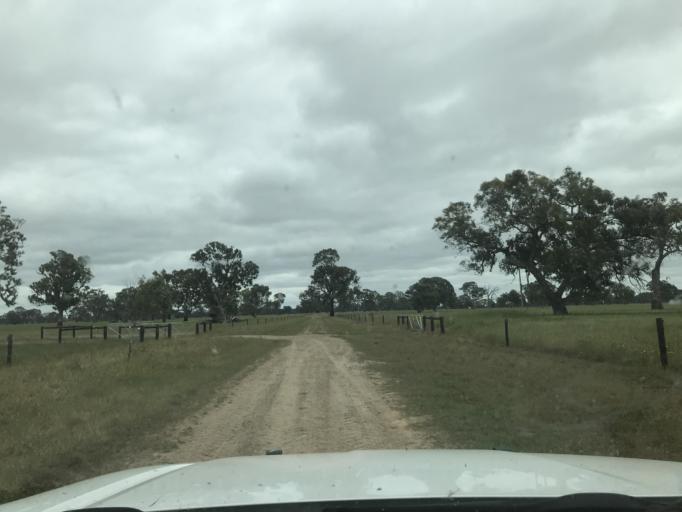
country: AU
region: South Australia
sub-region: Wattle Range
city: Penola
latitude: -37.1773
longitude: 141.0413
